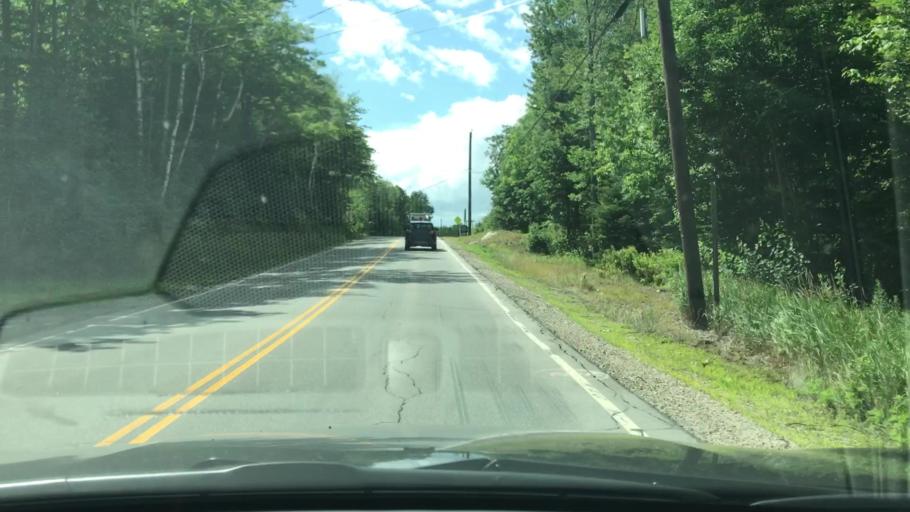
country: US
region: New Hampshire
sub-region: Coos County
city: Jefferson
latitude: 44.3622
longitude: -71.3833
